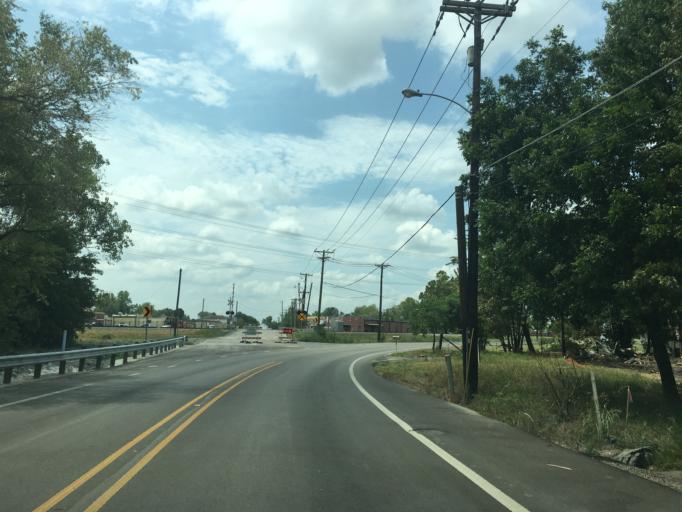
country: US
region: Texas
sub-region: Rockwall County
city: Fate
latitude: 32.9437
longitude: -96.3815
